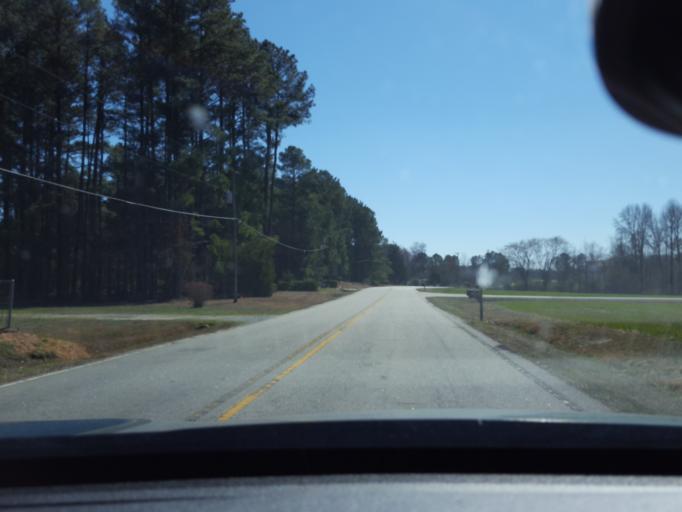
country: US
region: North Carolina
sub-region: Halifax County
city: South Rosemary
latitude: 36.3827
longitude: -77.9002
